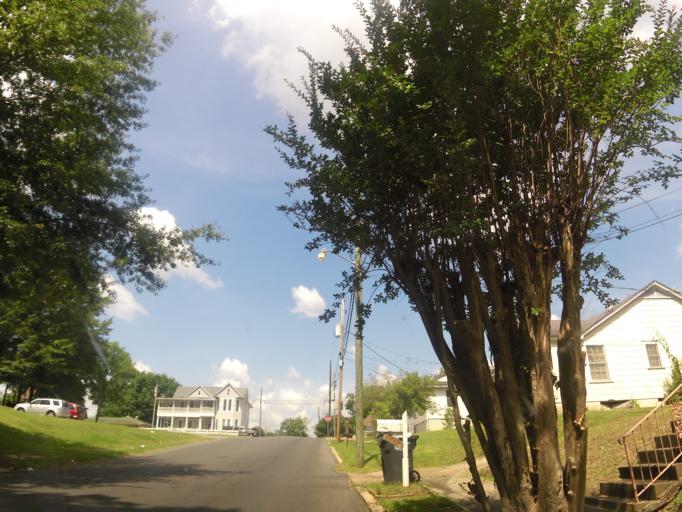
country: US
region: Mississippi
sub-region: Lauderdale County
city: Meridian
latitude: 32.3766
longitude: -88.7005
